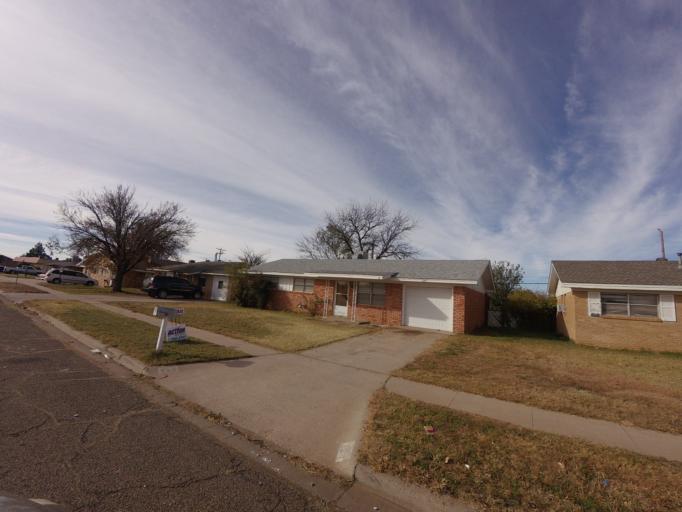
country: US
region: New Mexico
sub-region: Curry County
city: Clovis
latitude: 34.4204
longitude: -103.2235
